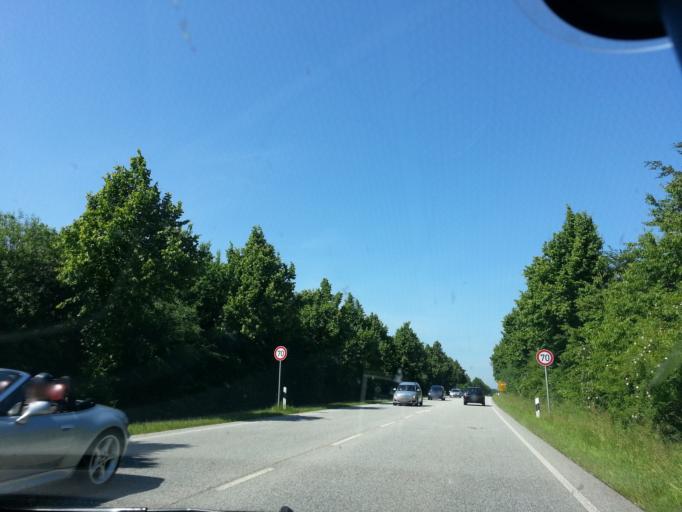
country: DE
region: Schleswig-Holstein
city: Harmsdorf
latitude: 53.6853
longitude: 10.7289
